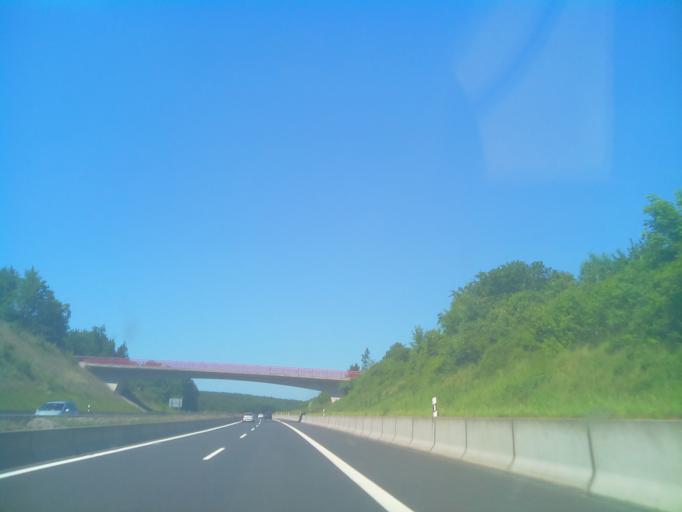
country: DE
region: Bavaria
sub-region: Regierungsbezirk Unterfranken
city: Rannungen
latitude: 50.1587
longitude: 10.1774
